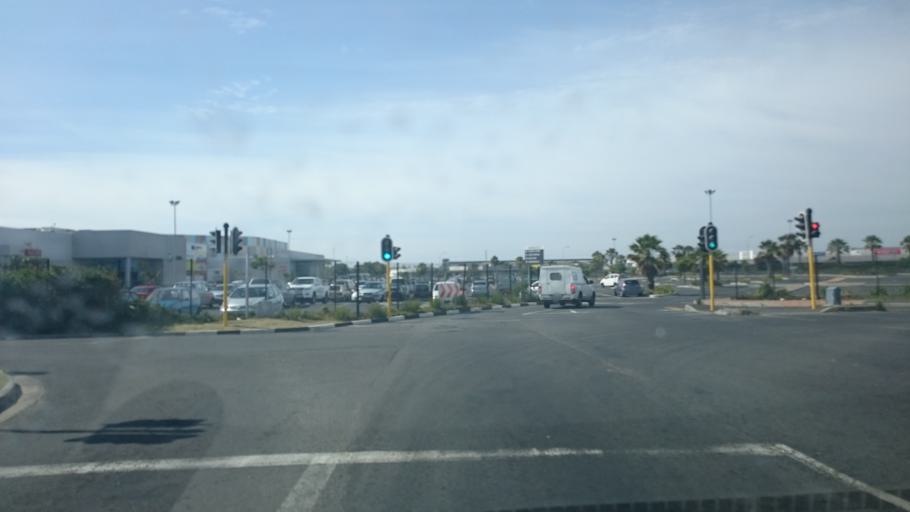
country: ZA
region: Western Cape
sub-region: City of Cape Town
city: Lansdowne
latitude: -34.0183
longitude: 18.5160
